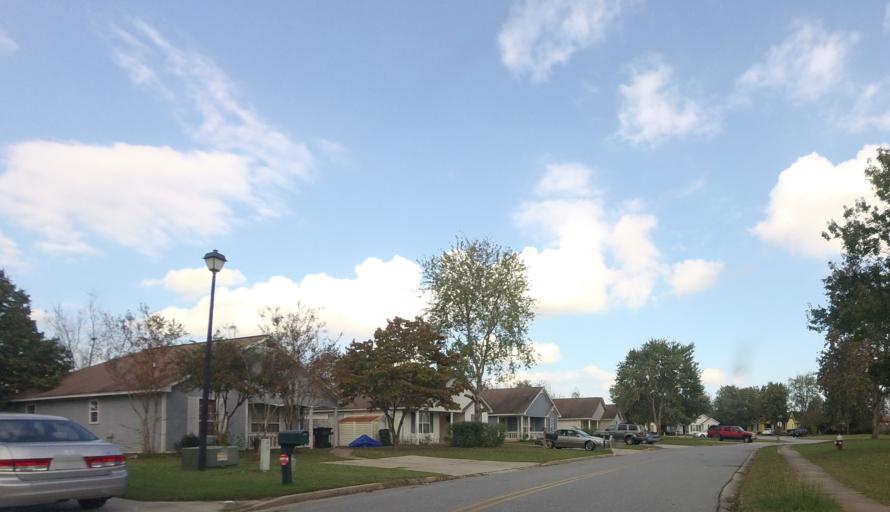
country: US
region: Georgia
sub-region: Houston County
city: Centerville
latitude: 32.6347
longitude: -83.6473
